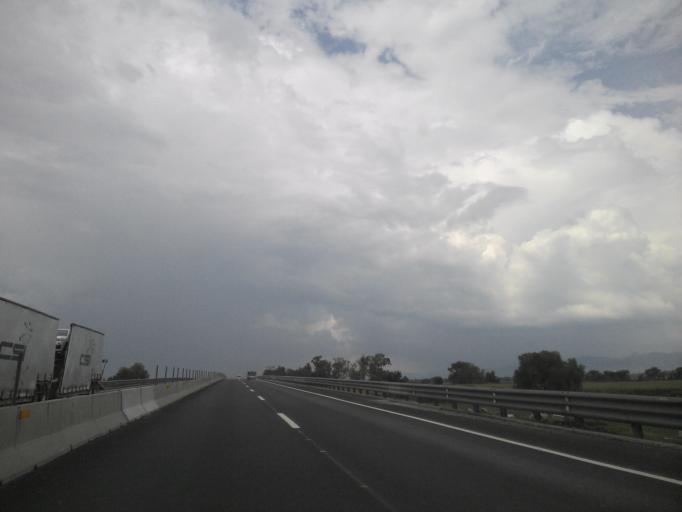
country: MX
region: Hidalgo
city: El Llano
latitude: 20.0862
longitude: -99.3227
